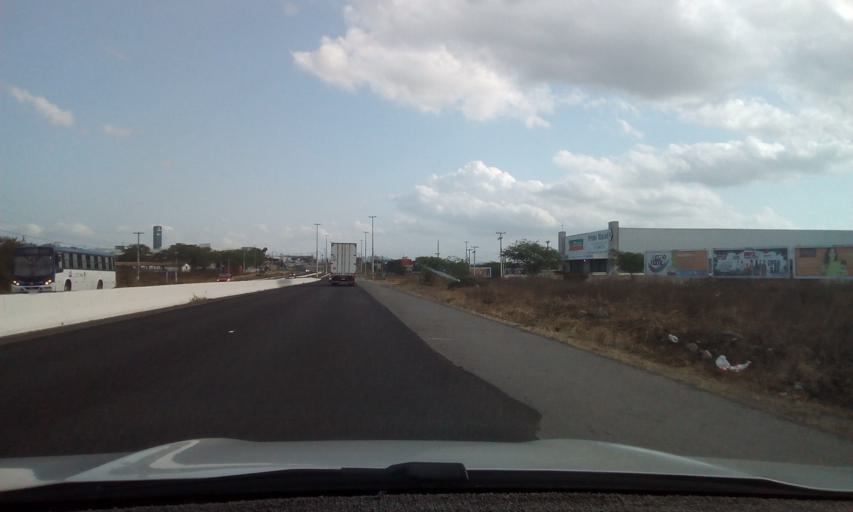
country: BR
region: Pernambuco
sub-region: Caruaru
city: Caruaru
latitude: -8.2398
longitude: -35.9756
